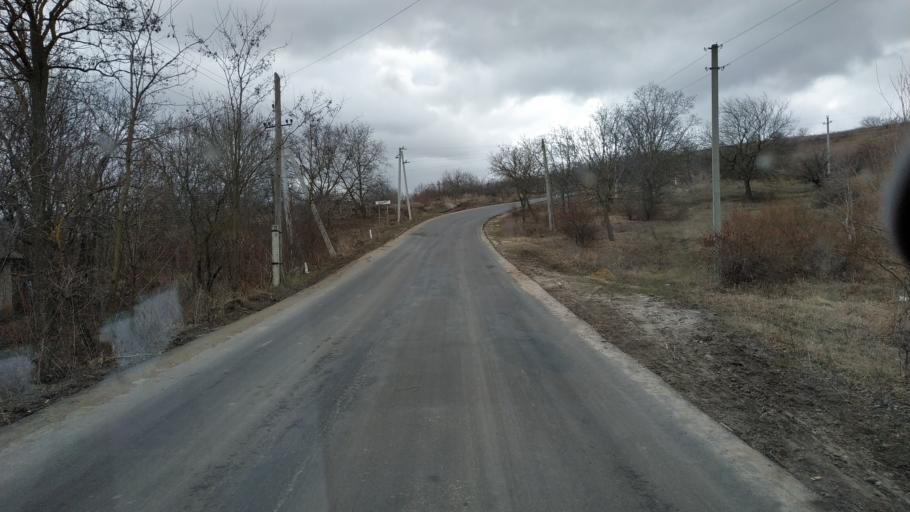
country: MD
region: Stinga Nistrului
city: Bucovat
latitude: 47.2224
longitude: 28.4254
